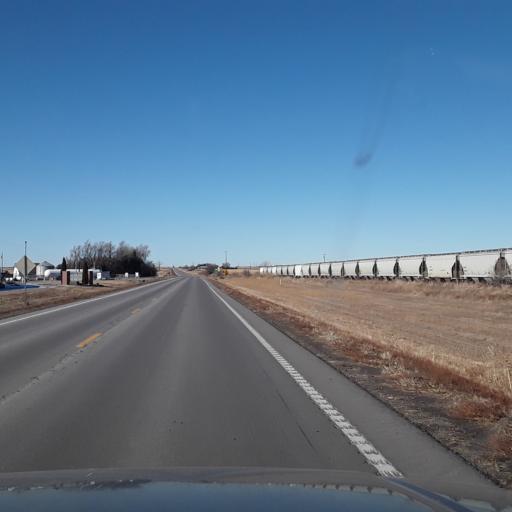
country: US
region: Nebraska
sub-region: Gosper County
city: Elwood
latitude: 40.5308
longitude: -99.6404
